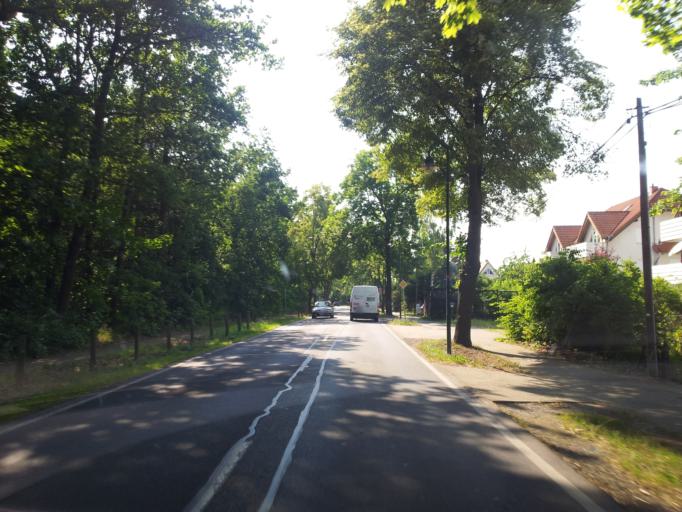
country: DE
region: Saxony
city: Ottendorf-Okrilla
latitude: 51.1257
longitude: 13.8229
